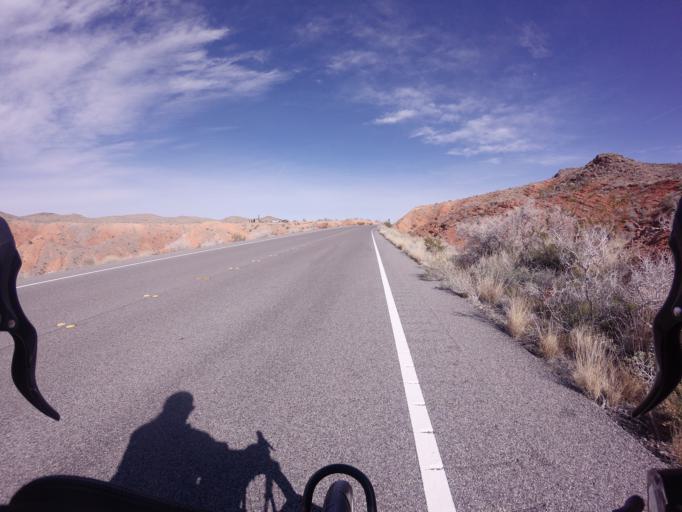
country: US
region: Nevada
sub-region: Clark County
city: Boulder City
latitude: 36.2262
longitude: -114.6223
